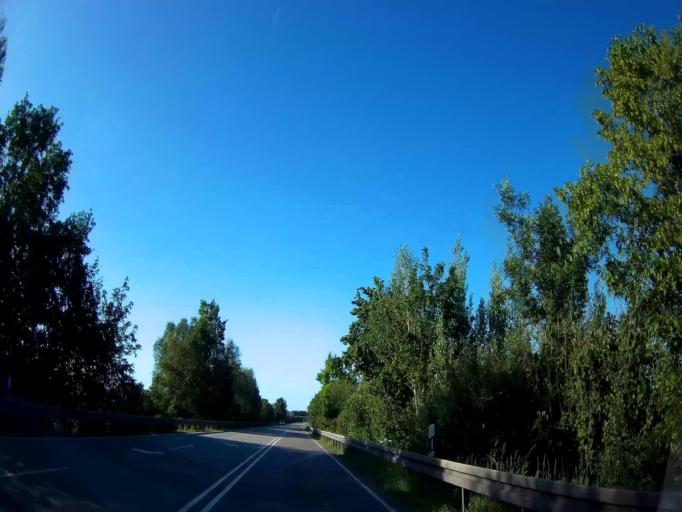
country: DE
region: Bavaria
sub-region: Lower Bavaria
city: Parkstetten
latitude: 48.9078
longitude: 12.6160
